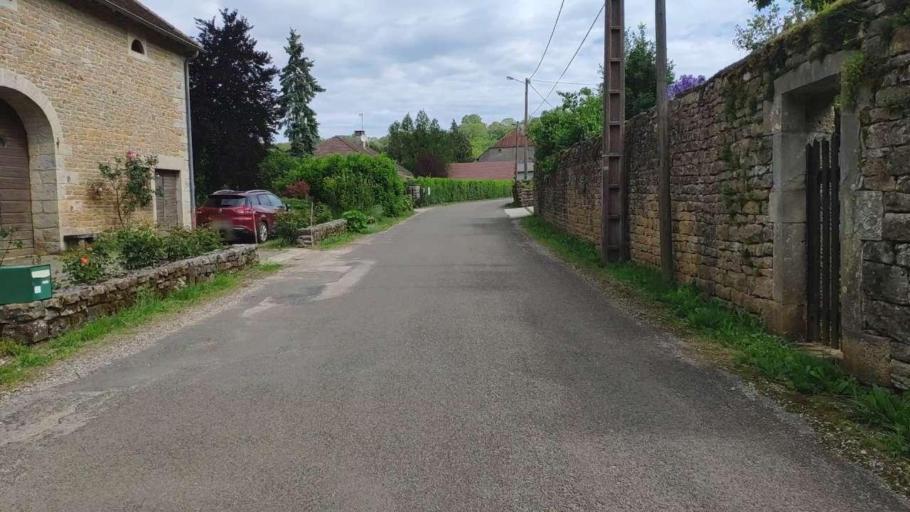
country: FR
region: Franche-Comte
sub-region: Departement du Jura
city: Poligny
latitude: 46.7699
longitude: 5.6234
